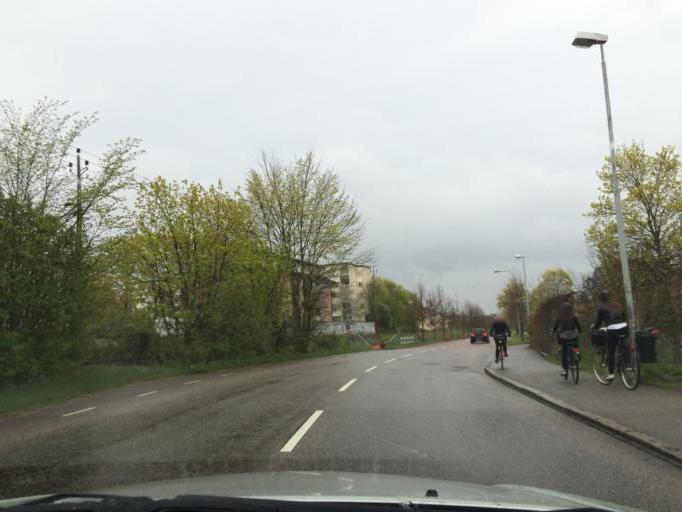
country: SE
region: Soedermanland
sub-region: Eskilstuna Kommun
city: Eskilstuna
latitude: 59.3623
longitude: 16.5099
